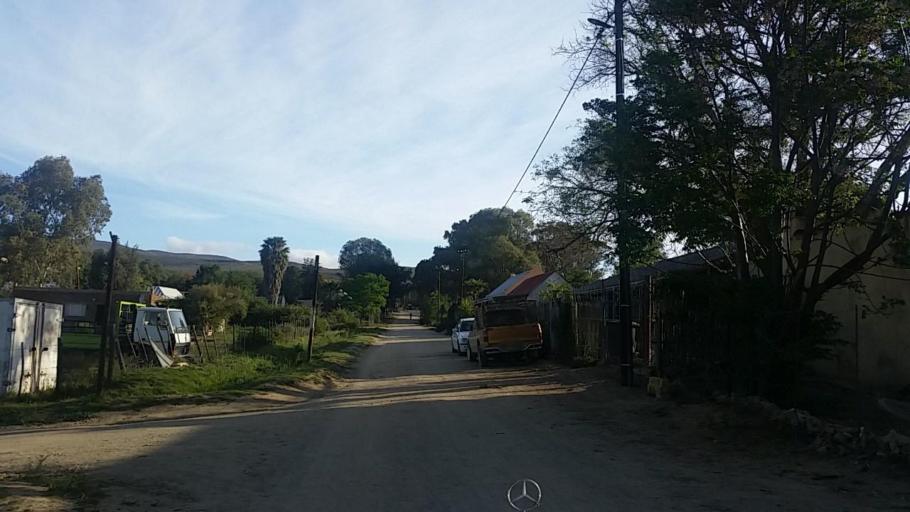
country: ZA
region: Western Cape
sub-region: Eden District Municipality
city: Knysna
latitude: -33.6571
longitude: 23.1184
